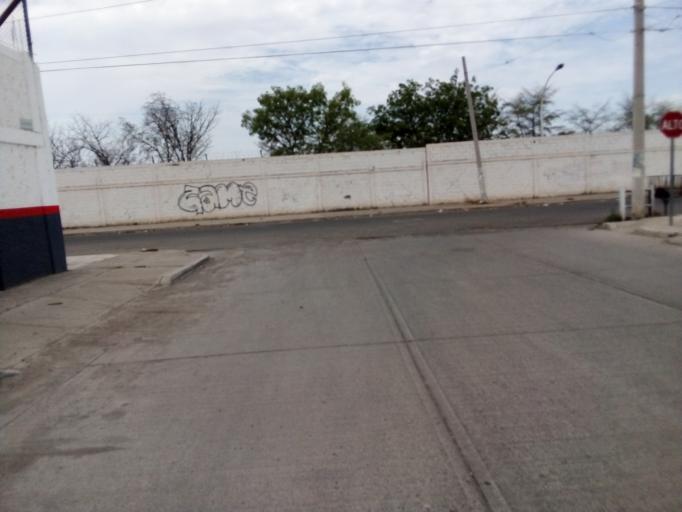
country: MX
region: Sinaloa
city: Culiacan
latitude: 24.7721
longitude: -107.4313
